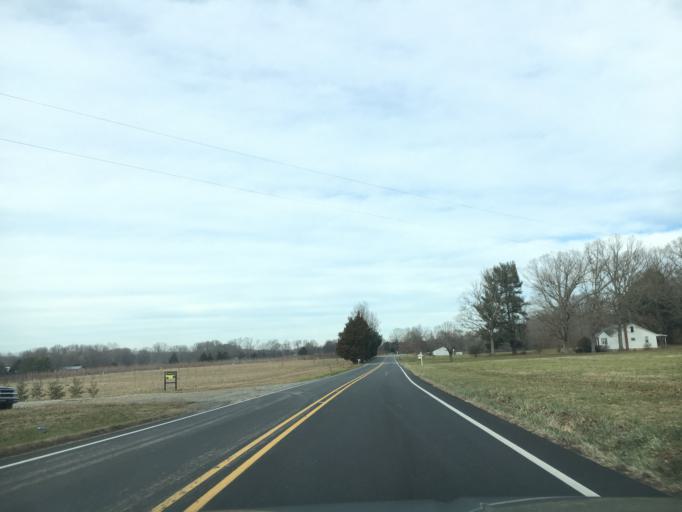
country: US
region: Virginia
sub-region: Goochland County
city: Goochland
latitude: 37.8226
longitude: -77.8884
